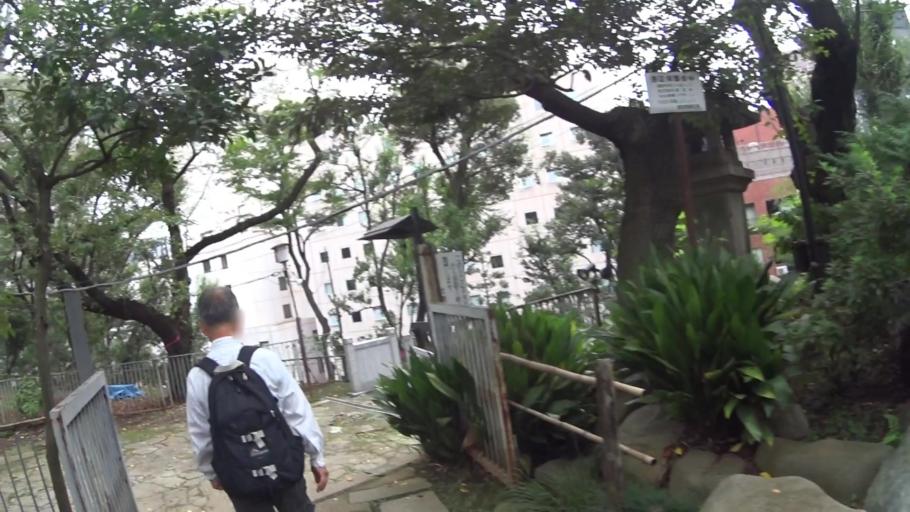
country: JP
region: Tokyo
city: Tokyo
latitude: 35.6650
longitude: 139.7489
